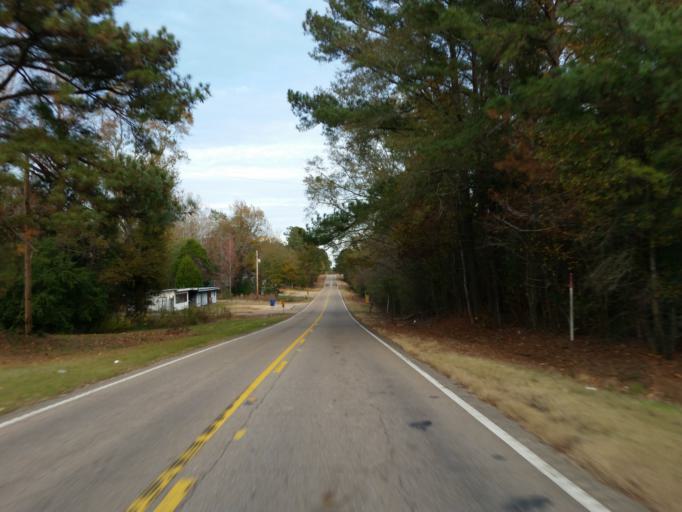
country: US
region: Mississippi
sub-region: Lauderdale County
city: Marion
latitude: 32.4225
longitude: -88.4803
